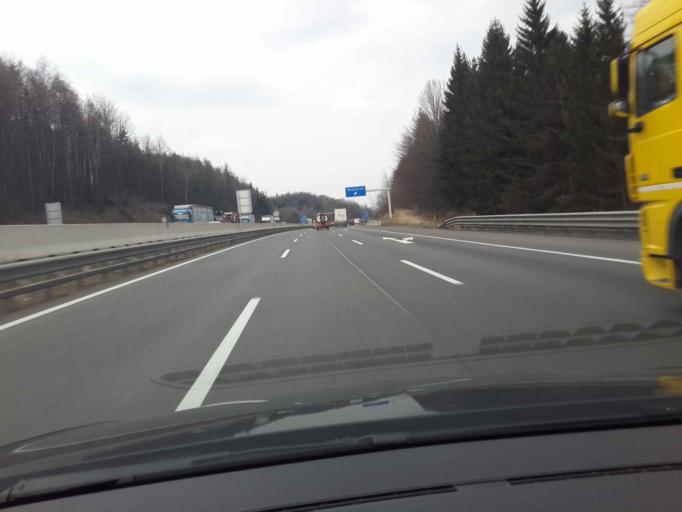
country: AT
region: Lower Austria
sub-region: Politischer Bezirk Sankt Polten
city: Eichgraben
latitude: 48.1288
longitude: 15.9712
